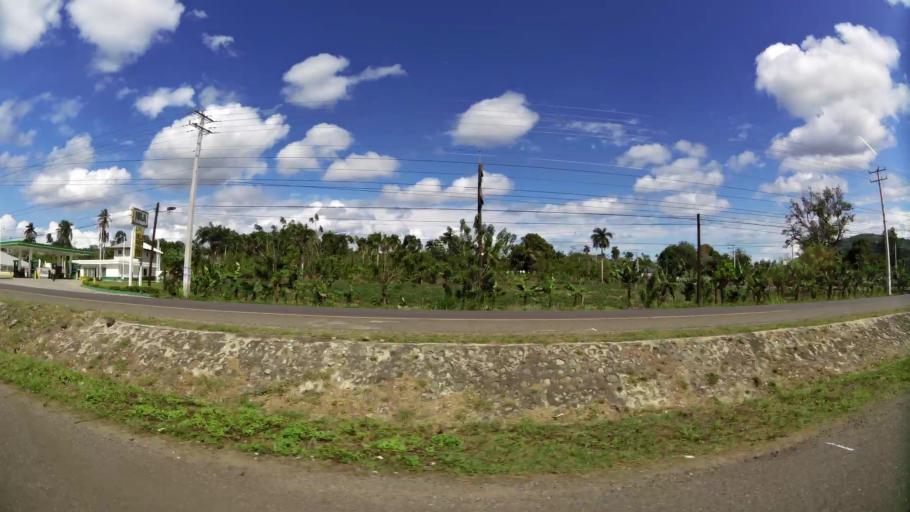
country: DO
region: La Vega
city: Rio Verde Arriba
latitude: 19.3194
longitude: -70.5872
